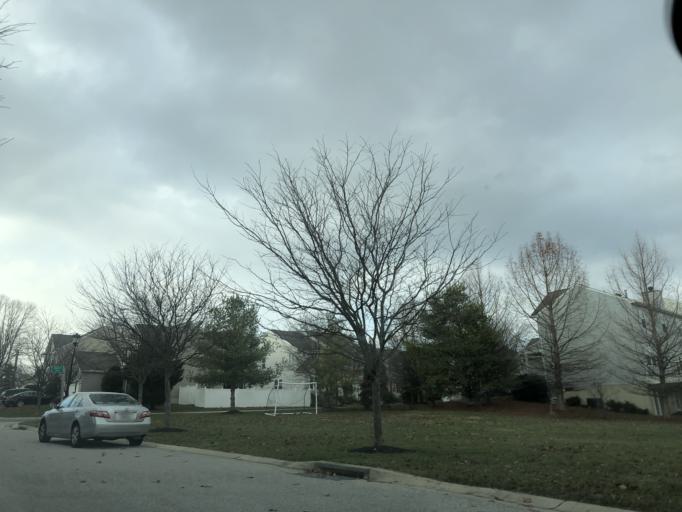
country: US
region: Maryland
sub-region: Howard County
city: Columbia
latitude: 39.2050
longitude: -76.8321
